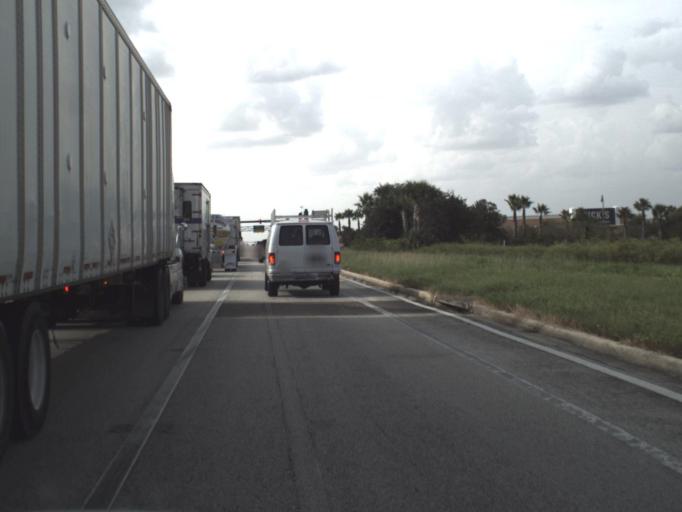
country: US
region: Florida
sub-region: Polk County
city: Davenport
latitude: 28.2236
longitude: -81.6443
